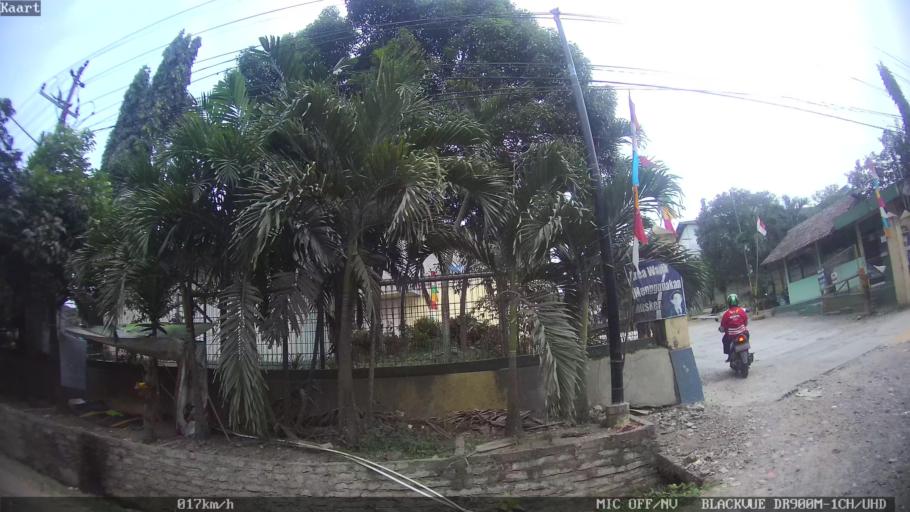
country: ID
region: Lampung
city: Panjang
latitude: -5.4188
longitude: 105.3330
